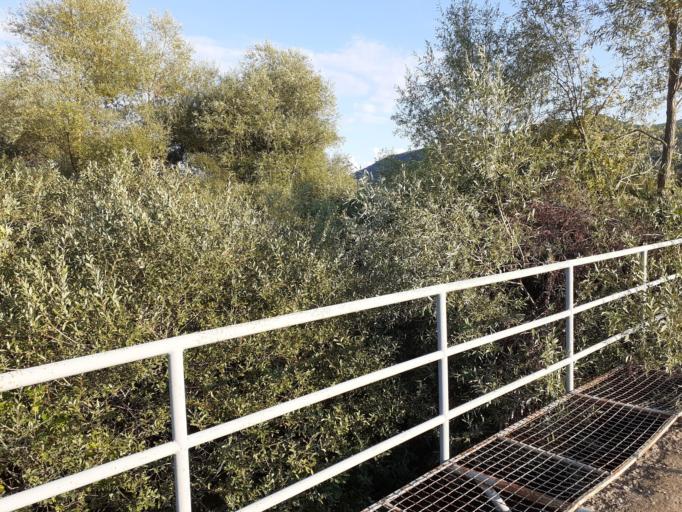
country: RS
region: Central Serbia
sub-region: Pirotski Okrug
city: Dimitrovgrad
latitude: 43.0078
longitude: 22.8185
